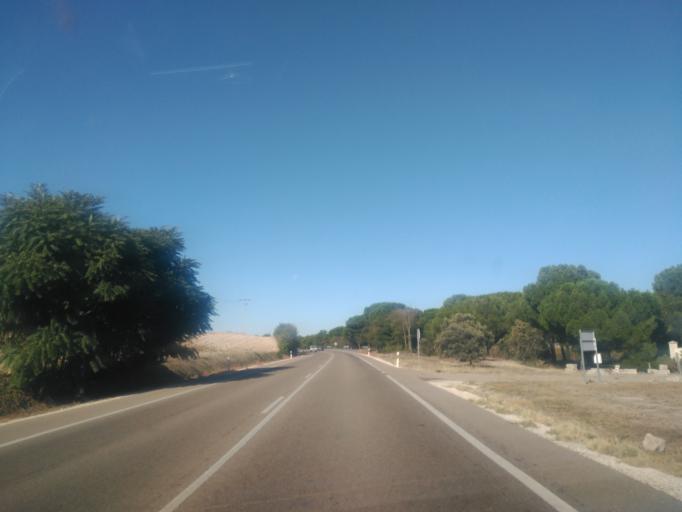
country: ES
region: Castille and Leon
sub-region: Provincia de Valladolid
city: Valbuena de Duero
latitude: 41.6279
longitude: -4.2856
